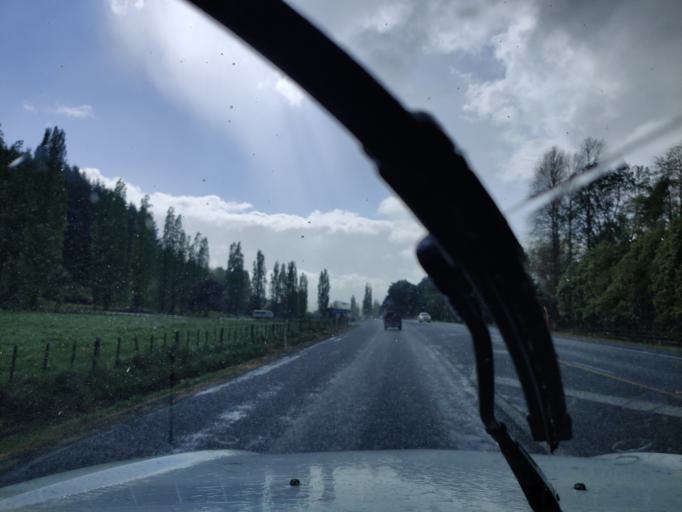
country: NZ
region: Waikato
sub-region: Matamata-Piako District
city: Matamata
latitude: -37.9521
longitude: 175.6268
